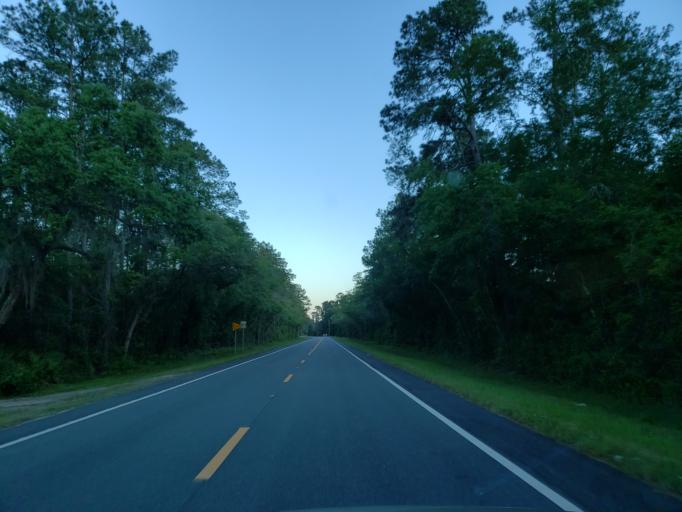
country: US
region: Georgia
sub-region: Echols County
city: Statenville
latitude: 30.5772
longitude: -83.1672
